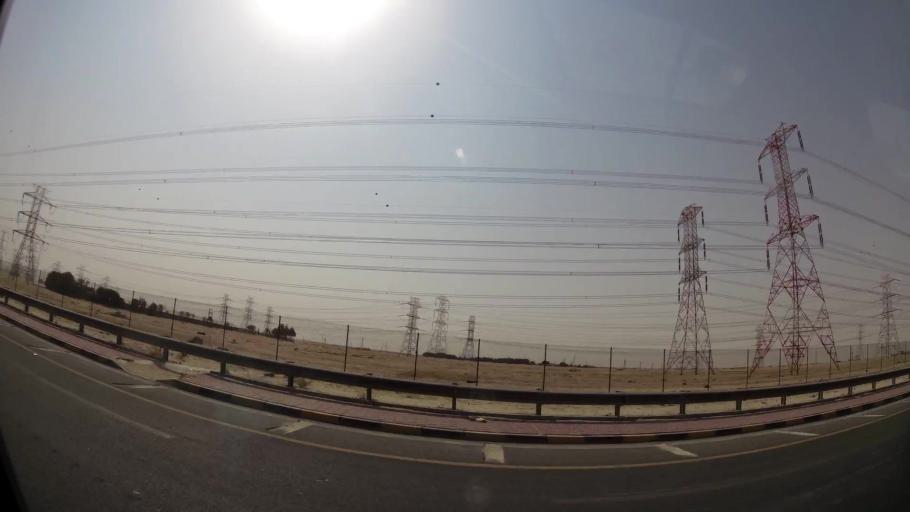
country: KW
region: Muhafazat al Jahra'
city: Al Jahra'
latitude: 29.3012
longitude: 47.6867
